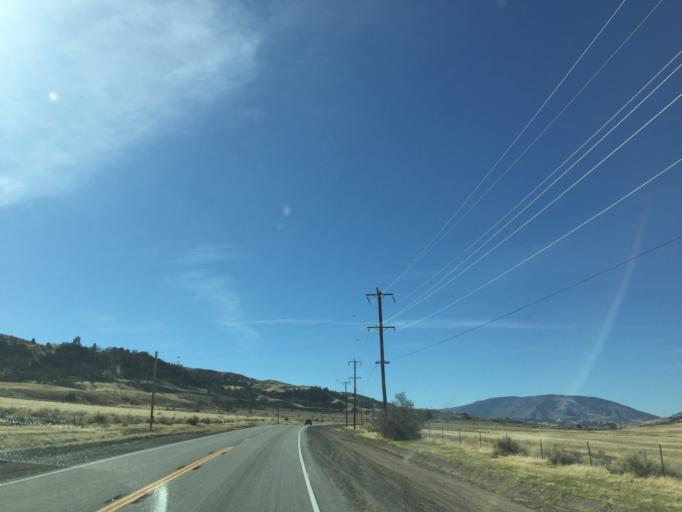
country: US
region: California
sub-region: Kern County
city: Lebec
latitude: 34.7658
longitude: -118.7123
